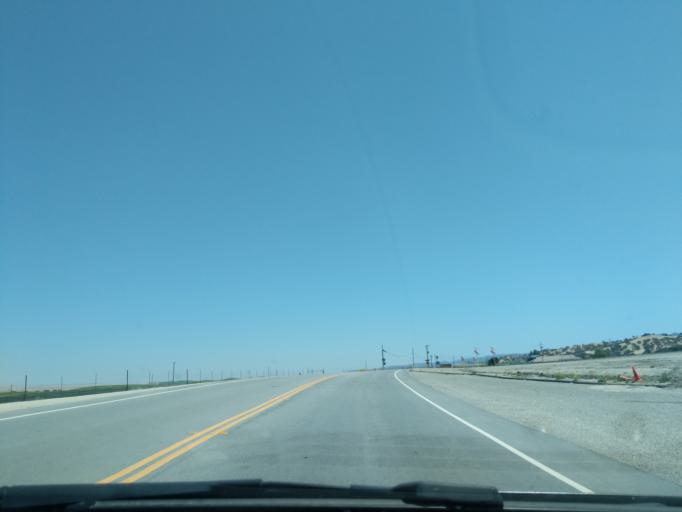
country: US
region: California
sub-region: Monterey County
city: King City
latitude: 36.1957
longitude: -121.1460
